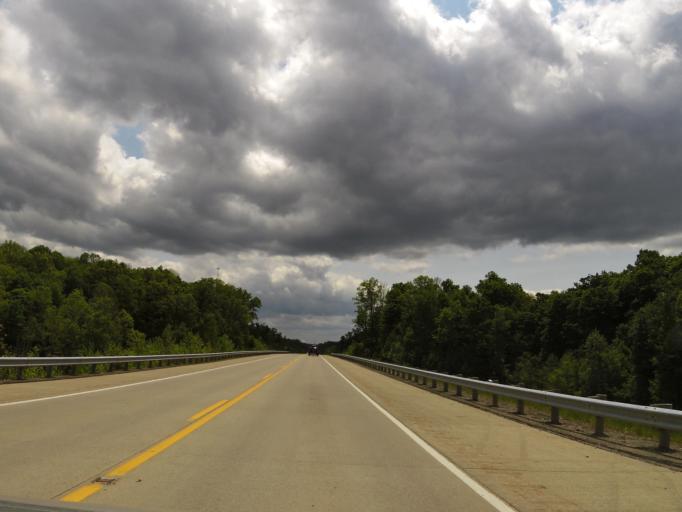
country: US
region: Ohio
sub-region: Meigs County
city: Pomeroy
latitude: 39.1811
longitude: -82.0475
